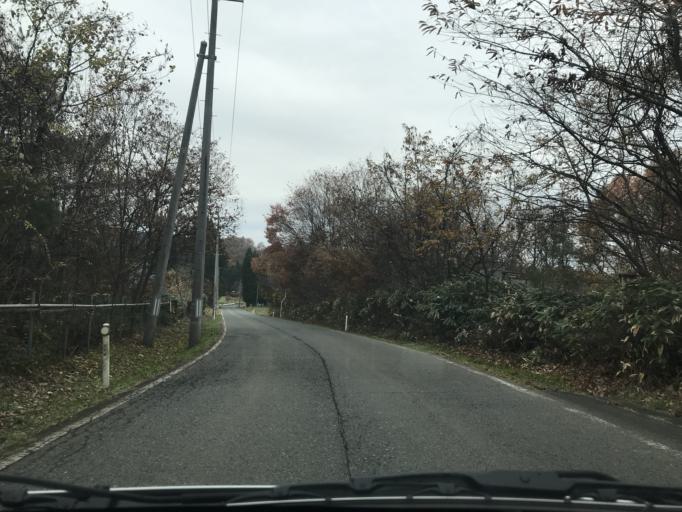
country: JP
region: Iwate
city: Kitakami
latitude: 39.2865
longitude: 141.1767
